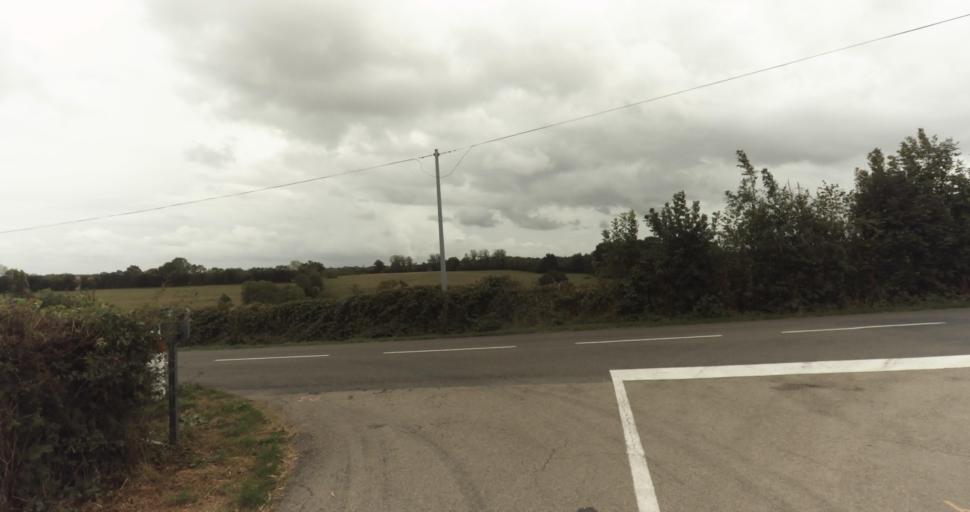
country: FR
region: Lower Normandy
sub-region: Departement de l'Orne
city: Gace
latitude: 48.8064
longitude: 0.3512
